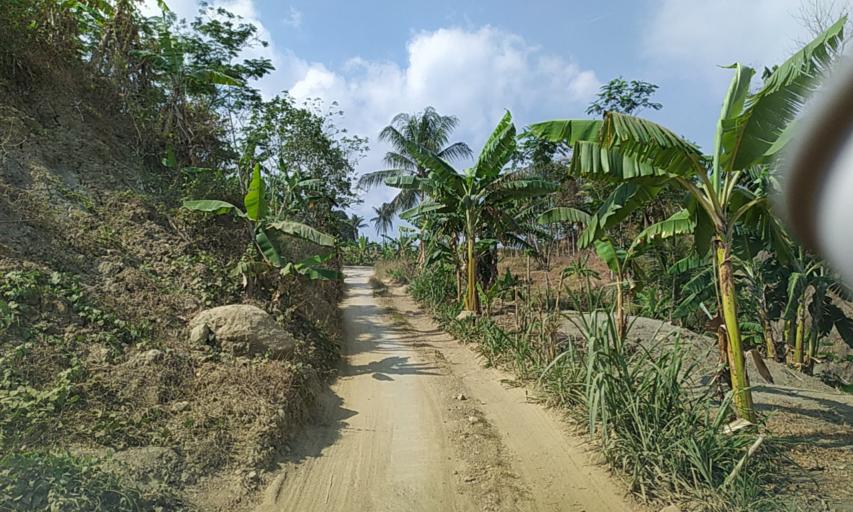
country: ID
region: Central Java
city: Jambuluwuk
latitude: -7.3293
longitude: 108.9010
